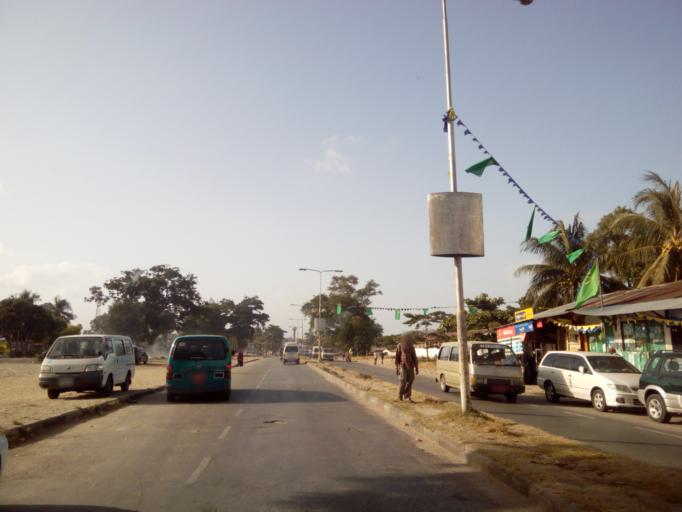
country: TZ
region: Zanzibar Urban/West
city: Zanzibar
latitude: -6.1632
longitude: 39.2040
